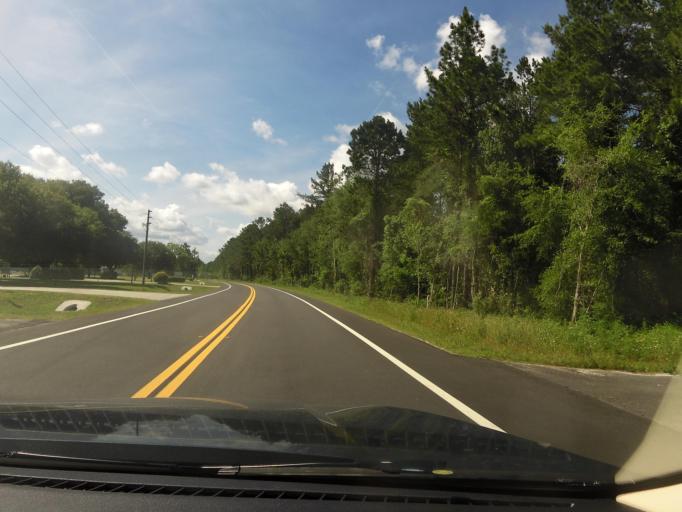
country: US
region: Florida
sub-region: Nassau County
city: Hilliard
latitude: 30.6664
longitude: -81.9040
